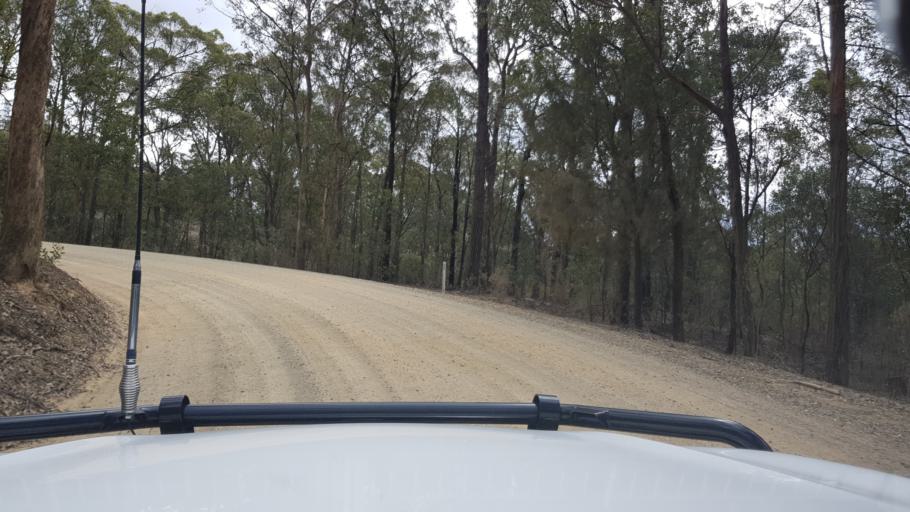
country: AU
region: Victoria
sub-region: East Gippsland
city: Bairnsdale
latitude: -37.6984
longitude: 147.5767
